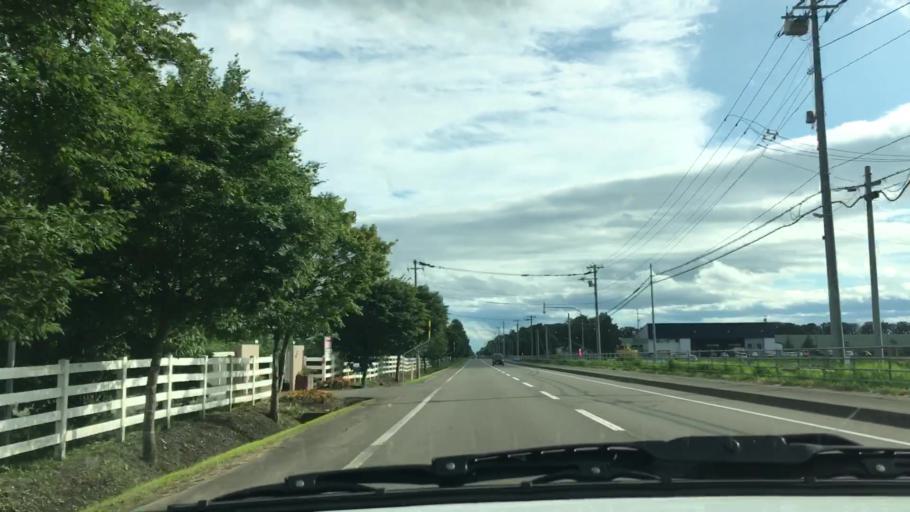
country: JP
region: Hokkaido
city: Otofuke
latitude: 43.2526
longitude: 143.2996
